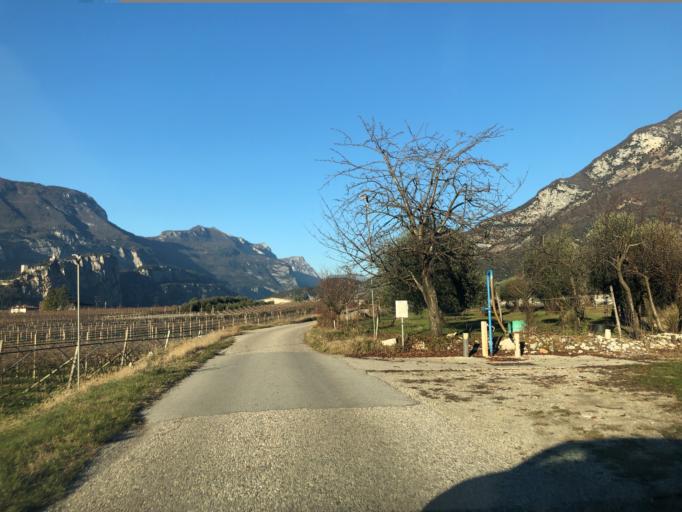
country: IT
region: Trentino-Alto Adige
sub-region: Provincia di Trento
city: Bolognano-Vignole
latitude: 45.9041
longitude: 10.8945
